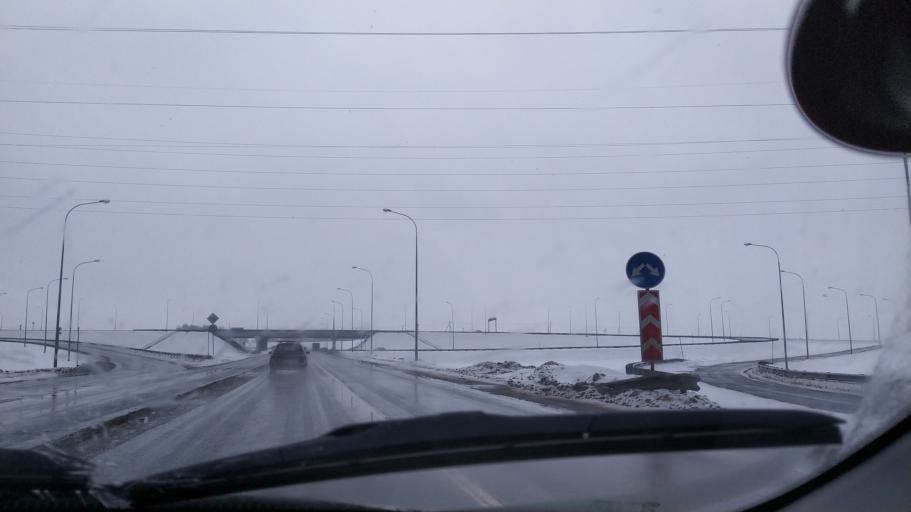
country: RU
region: Tatarstan
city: Aysha
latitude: 55.8736
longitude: 48.6602
